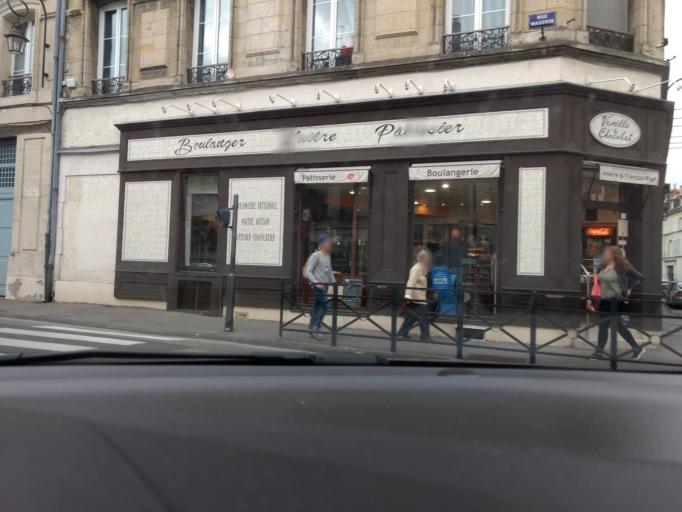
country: FR
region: Picardie
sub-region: Departement de l'Oise
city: Compiegne
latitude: 49.4161
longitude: 2.8273
